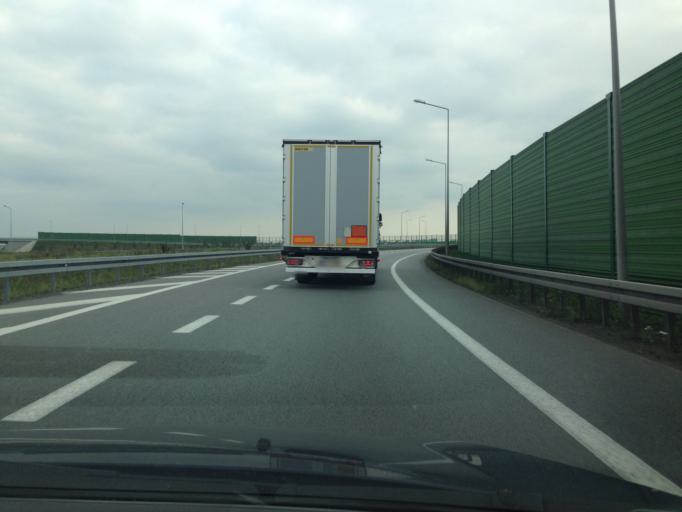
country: PL
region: Greater Poland Voivodeship
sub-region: Powiat poznanski
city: Kleszczewo
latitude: 52.3186
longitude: 17.1236
